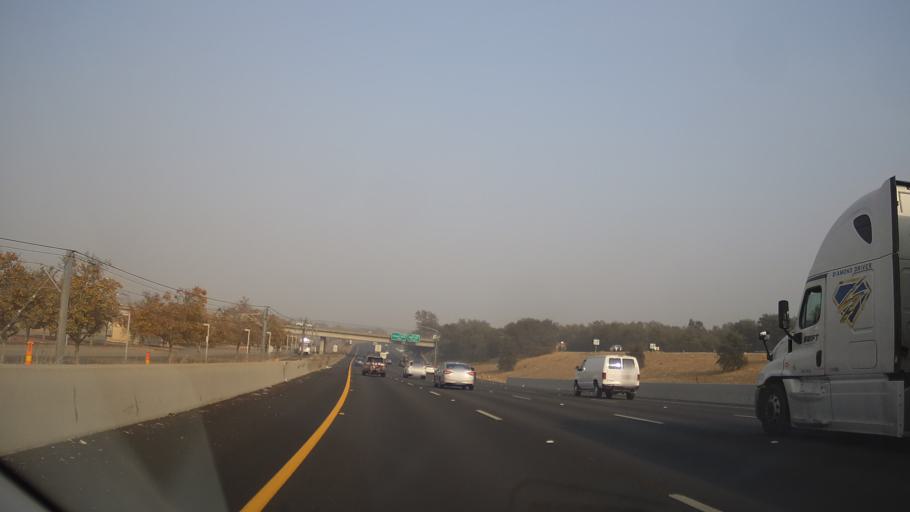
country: US
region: California
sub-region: Sacramento County
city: Arden-Arcade
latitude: 38.6386
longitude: -121.4007
